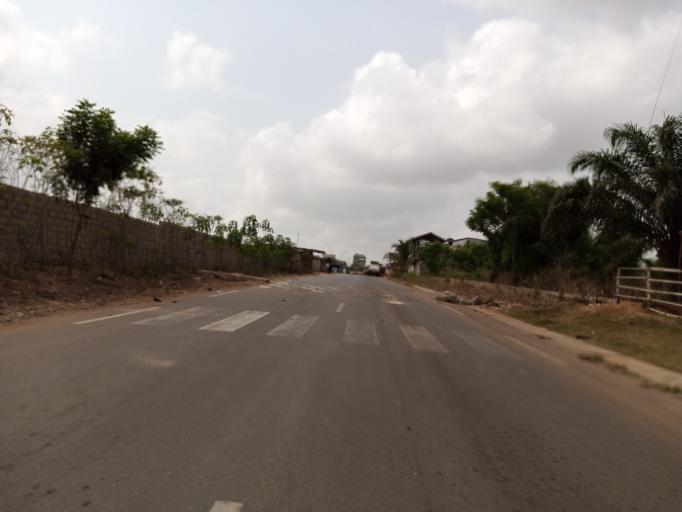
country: TG
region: Maritime
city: Lome
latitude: 6.2342
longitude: 1.0980
